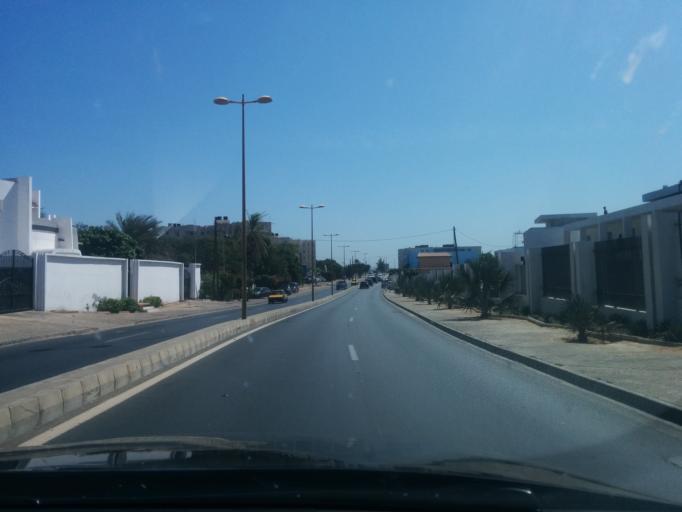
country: SN
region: Dakar
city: Mermoz Boabab
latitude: 14.7075
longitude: -17.4845
